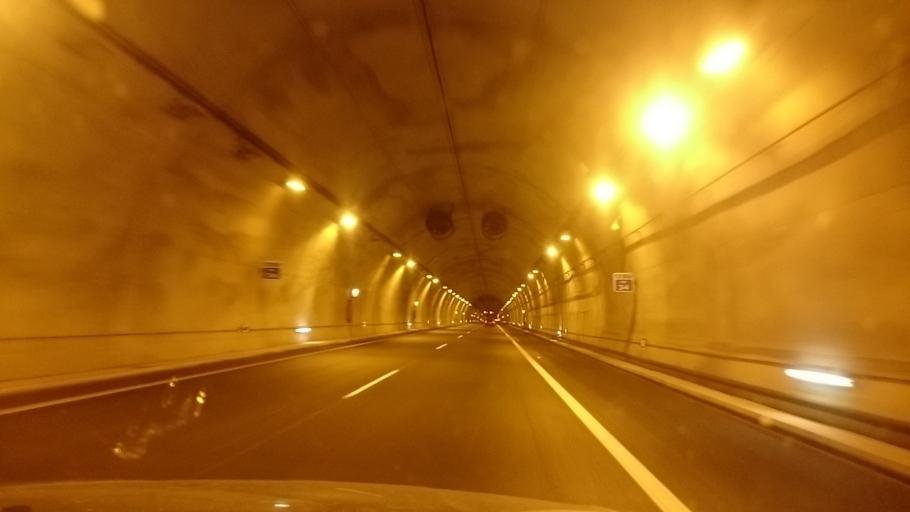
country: ES
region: Asturias
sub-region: Province of Asturias
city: Norena
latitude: 43.3481
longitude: -5.7202
